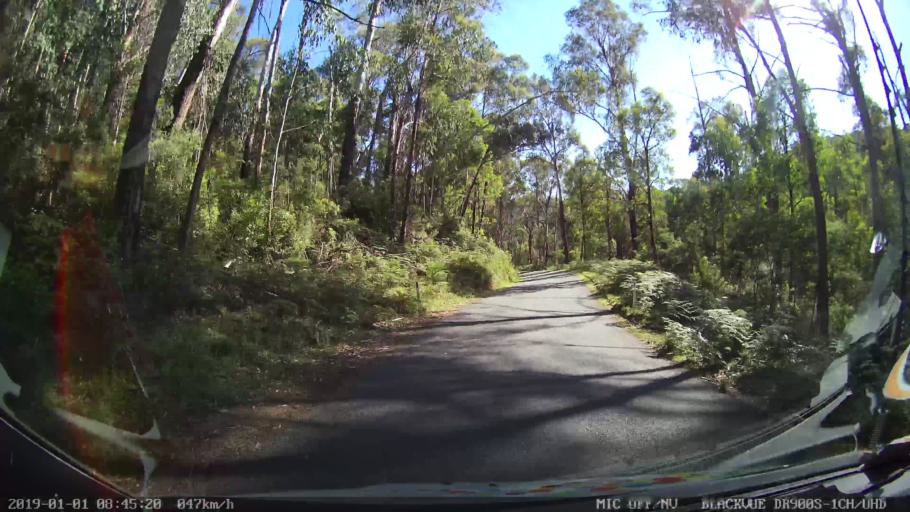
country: AU
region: New South Wales
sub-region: Snowy River
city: Jindabyne
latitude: -36.3061
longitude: 148.1878
